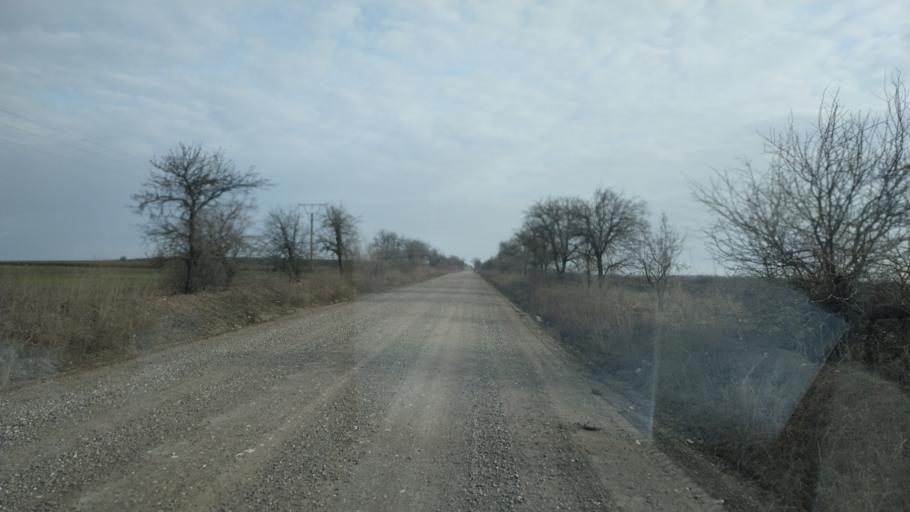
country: MD
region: Chisinau
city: Vadul lui Voda
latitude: 46.9833
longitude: 29.0851
